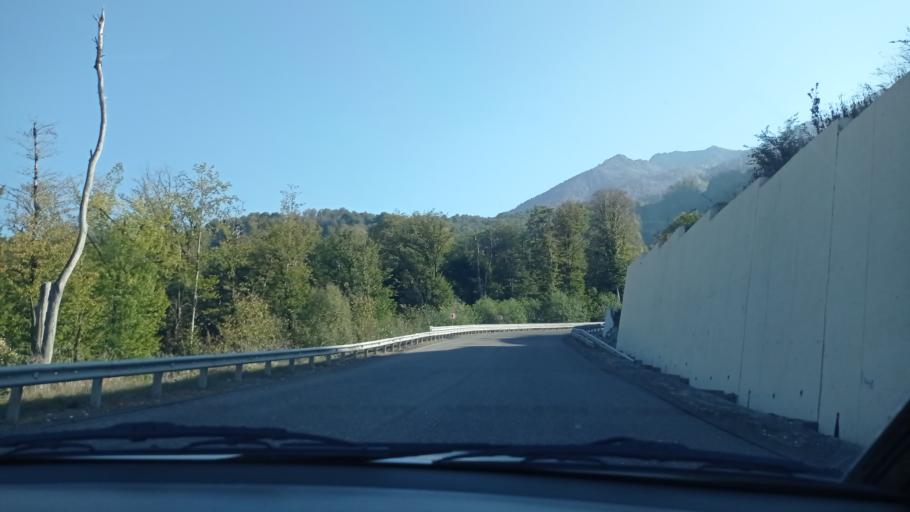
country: RU
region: Krasnodarskiy
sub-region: Sochi City
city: Krasnaya Polyana
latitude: 43.6705
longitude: 40.2894
